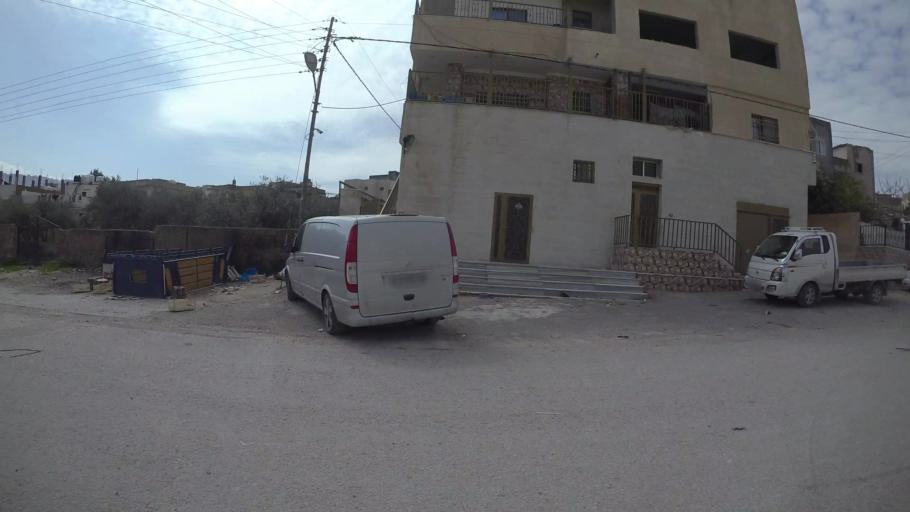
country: JO
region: Amman
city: Al Jubayhah
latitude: 32.0679
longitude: 35.8322
